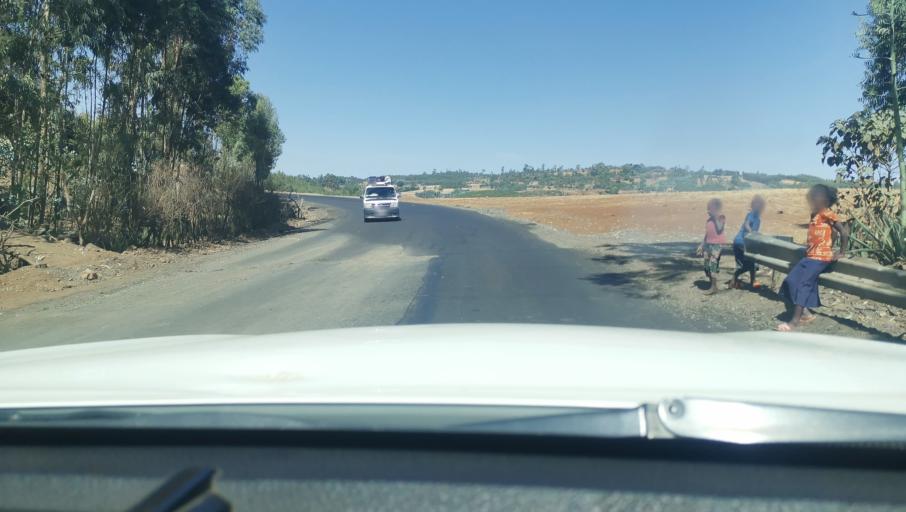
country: ET
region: Oromiya
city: Gedo
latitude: 8.9723
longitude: 37.4905
